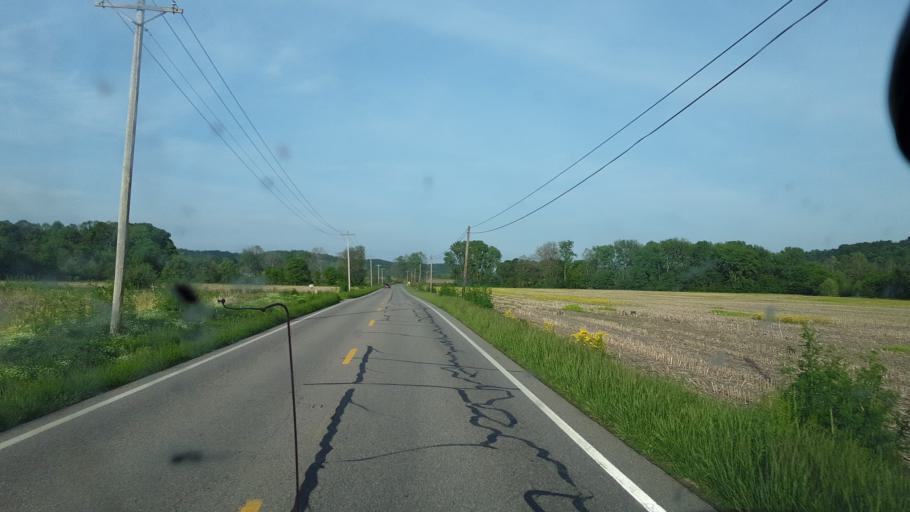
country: US
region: Ohio
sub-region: Ross County
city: Kingston
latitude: 39.4969
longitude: -82.7088
